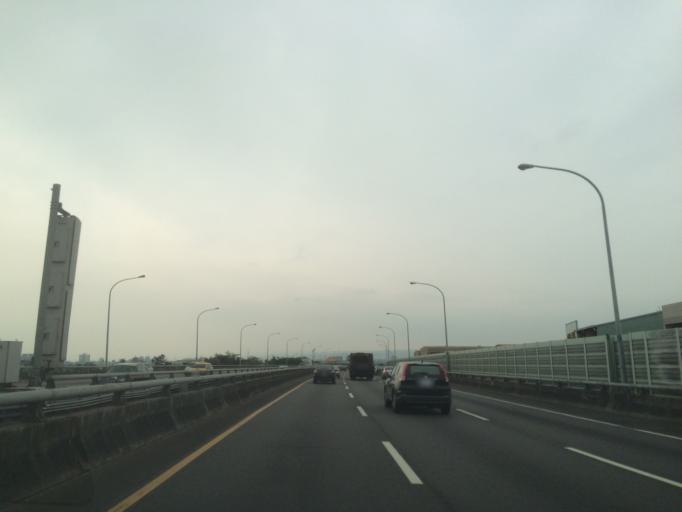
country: TW
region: Taiwan
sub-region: Taichung City
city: Taichung
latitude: 24.1382
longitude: 120.6225
